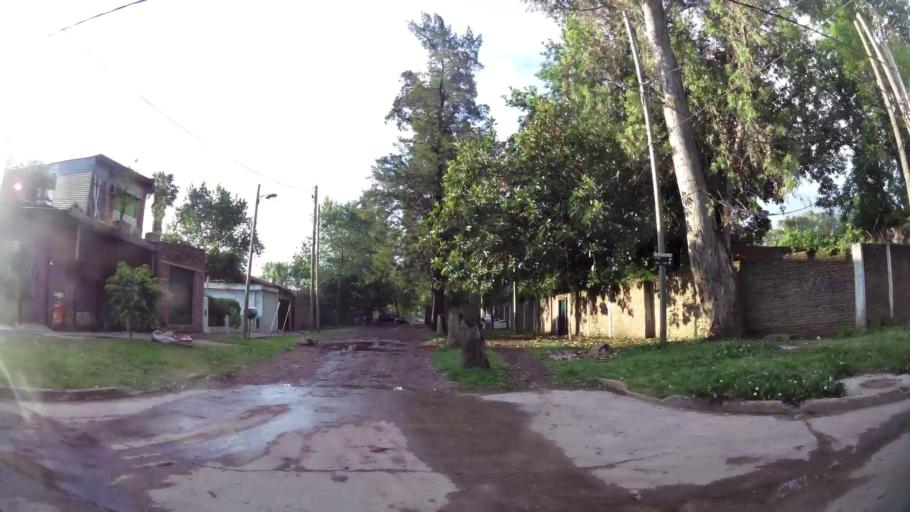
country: AR
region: Buenos Aires
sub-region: Partido de Lomas de Zamora
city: Lomas de Zamora
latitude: -34.7579
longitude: -58.3629
